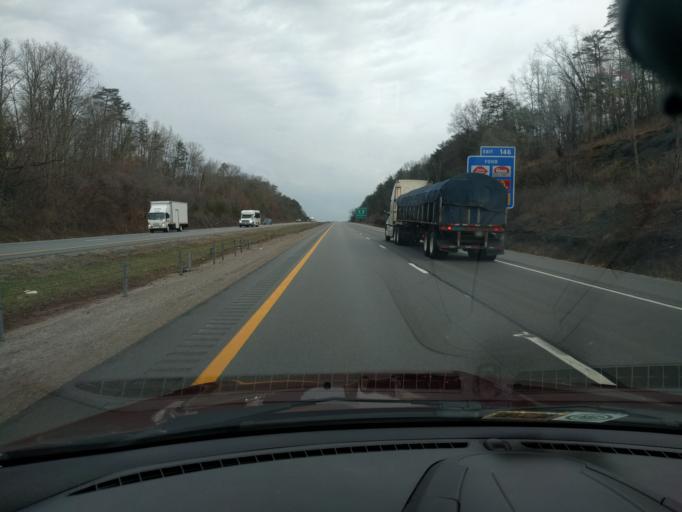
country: US
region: West Virginia
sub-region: Jackson County
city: Ravenswood
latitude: 38.9065
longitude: -81.7239
